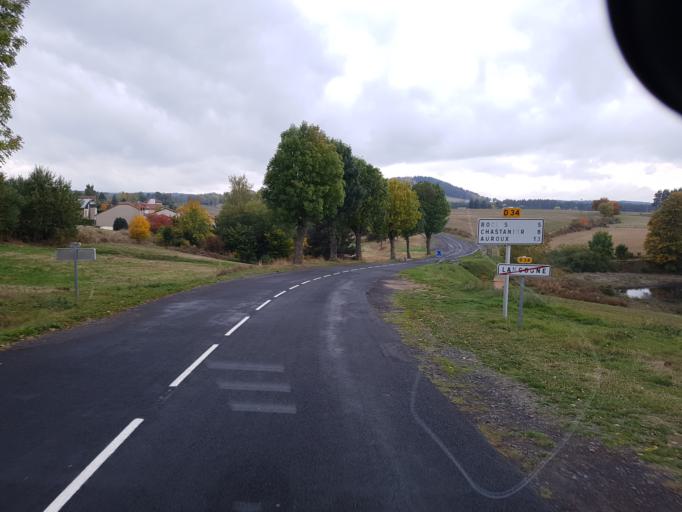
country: FR
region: Languedoc-Roussillon
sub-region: Departement de la Lozere
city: Langogne
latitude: 44.7235
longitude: 3.8383
